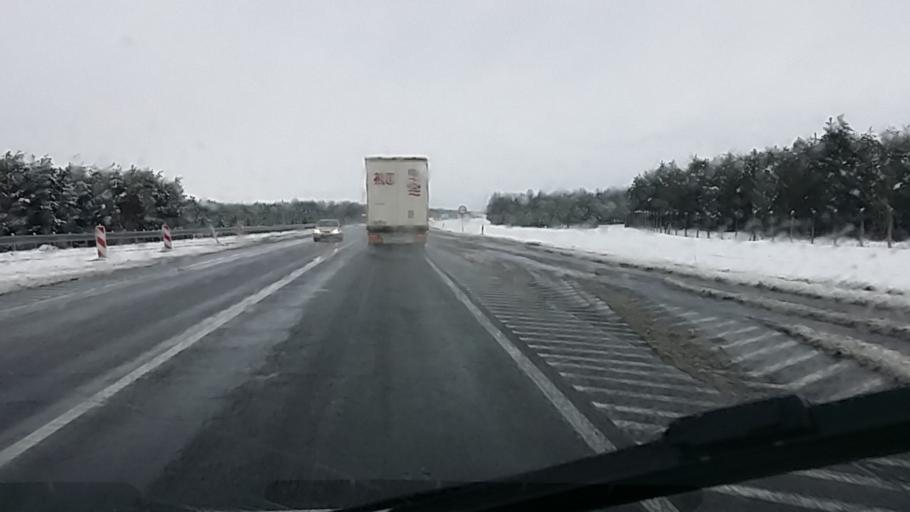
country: HU
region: Gyor-Moson-Sopron
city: Rajka
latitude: 47.9469
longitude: 17.1659
